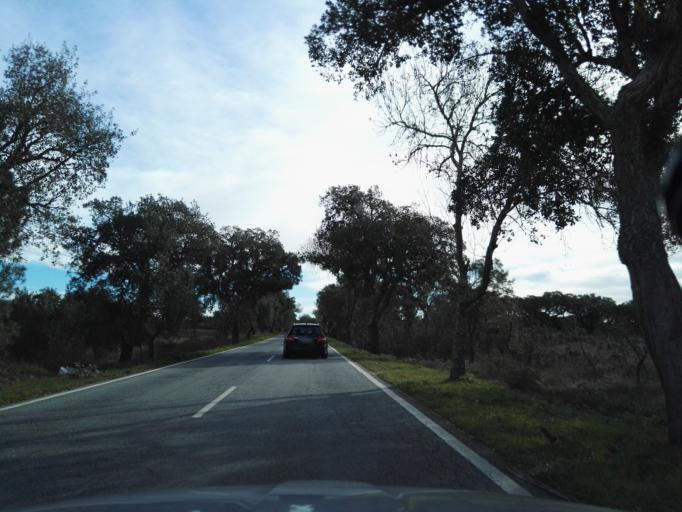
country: PT
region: Portalegre
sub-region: Nisa
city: Nisa
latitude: 39.5000
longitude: -7.6838
